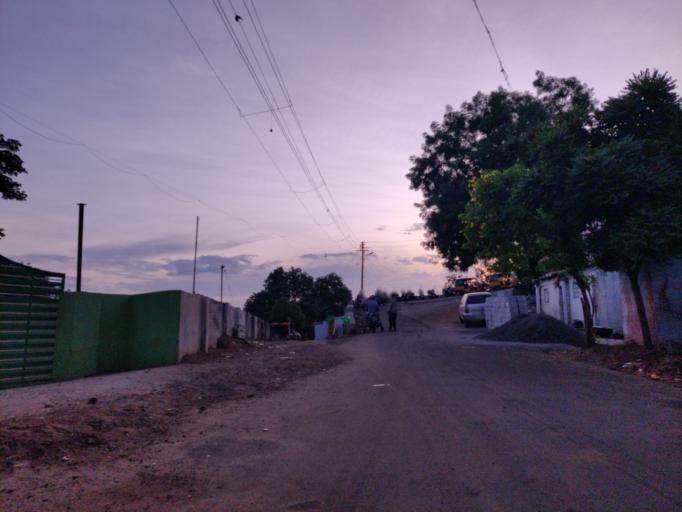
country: IN
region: Tamil Nadu
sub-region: Salem
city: Salem
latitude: 11.6218
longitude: 78.1487
